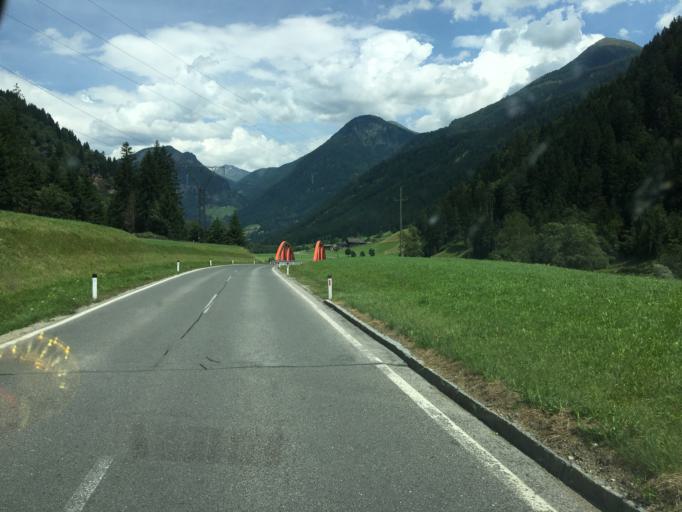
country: AT
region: Carinthia
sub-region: Politischer Bezirk Spittal an der Drau
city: Winklern
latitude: 46.8855
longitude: 12.8906
